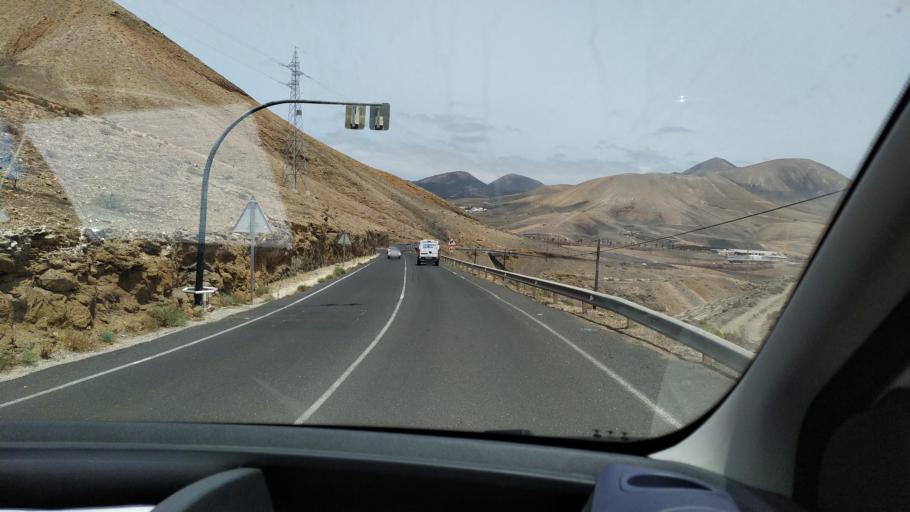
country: ES
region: Canary Islands
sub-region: Provincia de Las Palmas
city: Yaiza
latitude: 28.9312
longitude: -13.7483
